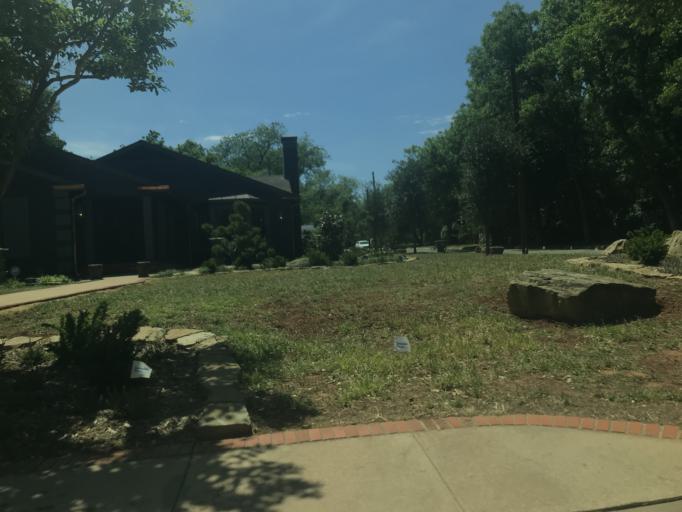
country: US
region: Texas
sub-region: Taylor County
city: Abilene
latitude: 32.4358
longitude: -99.7702
